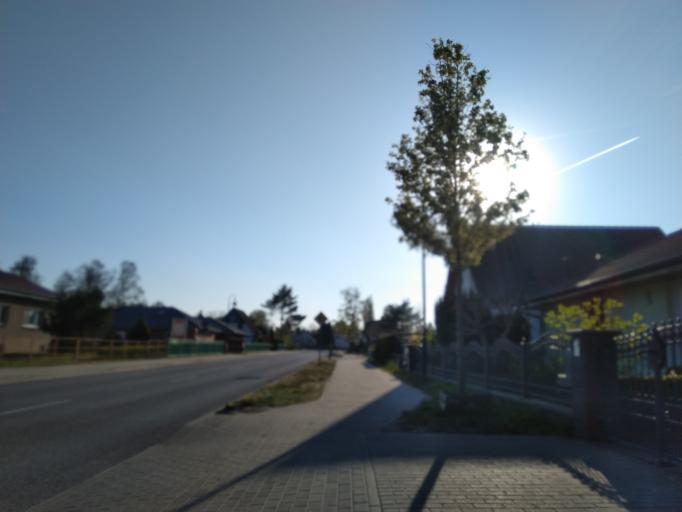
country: DE
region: Brandenburg
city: Bernau bei Berlin
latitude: 52.6593
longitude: 13.5537
